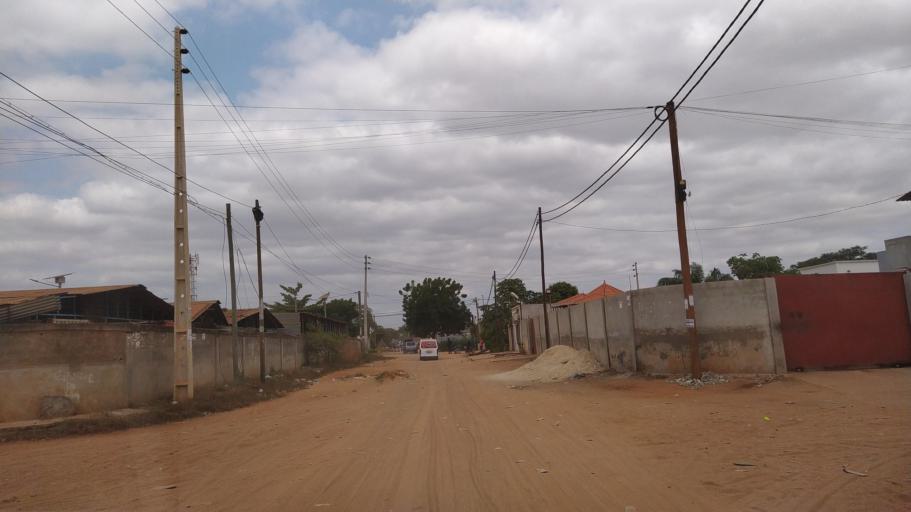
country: AO
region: Luanda
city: Luanda
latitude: -8.9282
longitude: 13.2614
